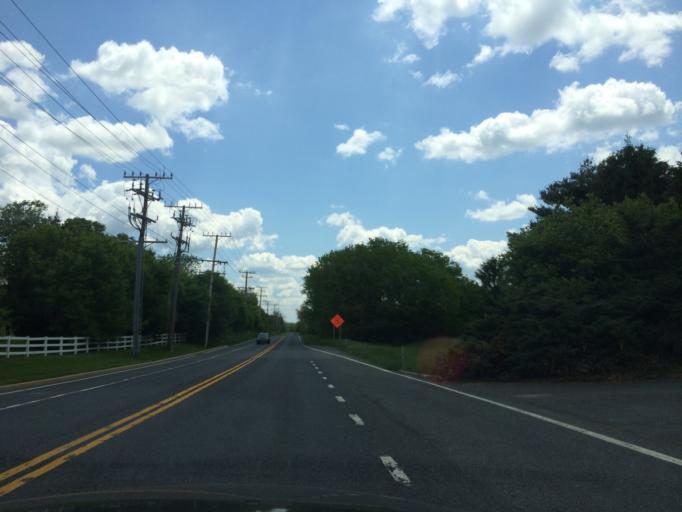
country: US
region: Maryland
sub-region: Carroll County
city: Sykesville
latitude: 39.3234
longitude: -77.0262
